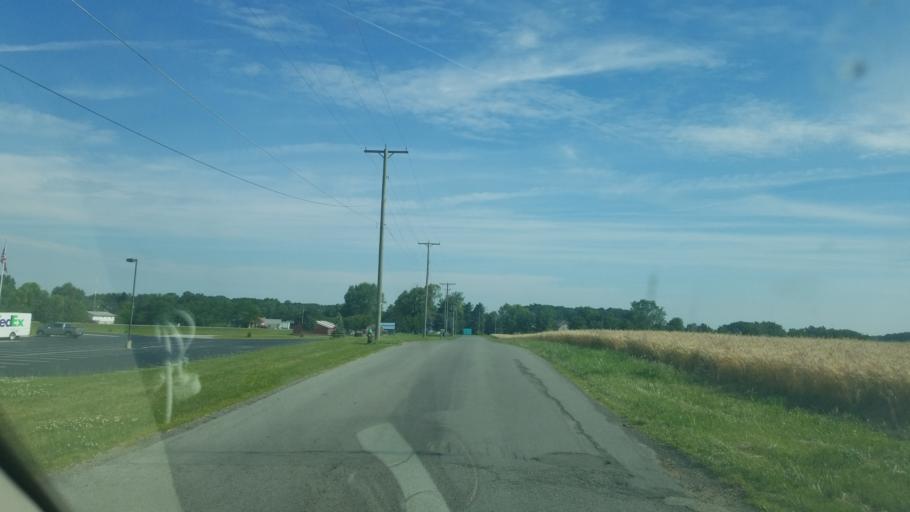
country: US
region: Ohio
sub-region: Wyandot County
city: Upper Sandusky
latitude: 40.8288
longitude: -83.2535
